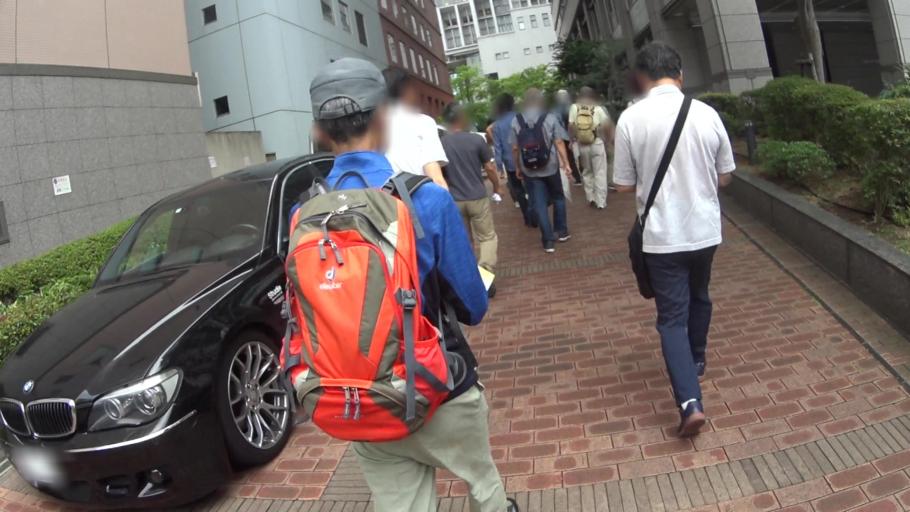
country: JP
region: Osaka
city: Osaka-shi
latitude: 34.7000
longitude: 135.4926
